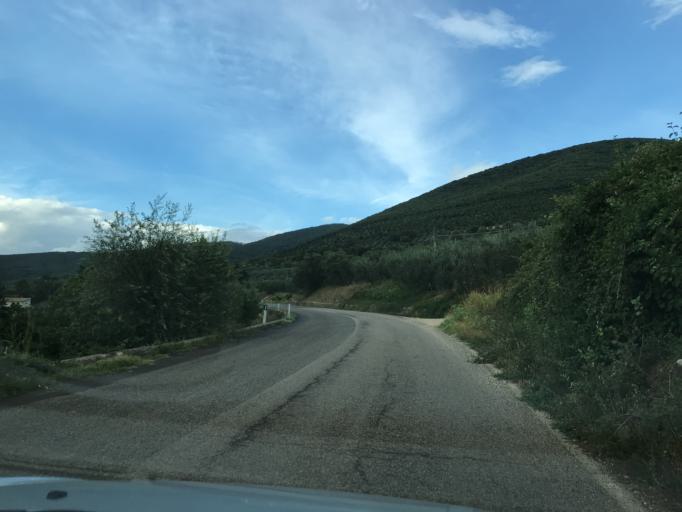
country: IT
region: Umbria
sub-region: Provincia di Terni
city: Montecchio
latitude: 42.6674
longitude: 12.2918
